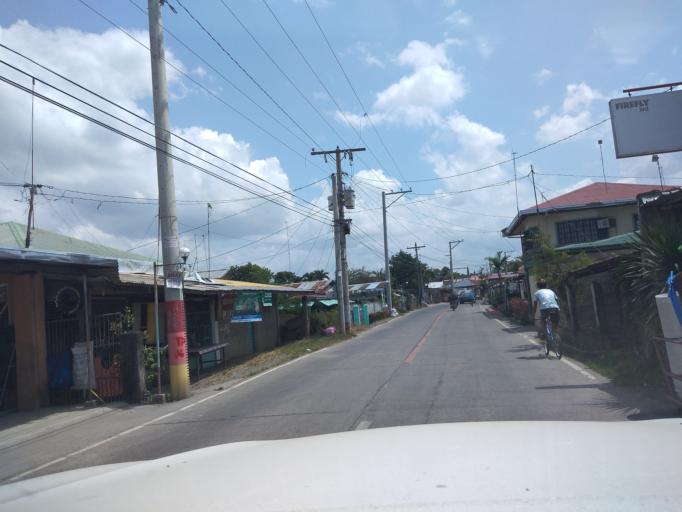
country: PH
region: Central Luzon
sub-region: Province of Pampanga
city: Lourdes
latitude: 15.0195
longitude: 120.8623
